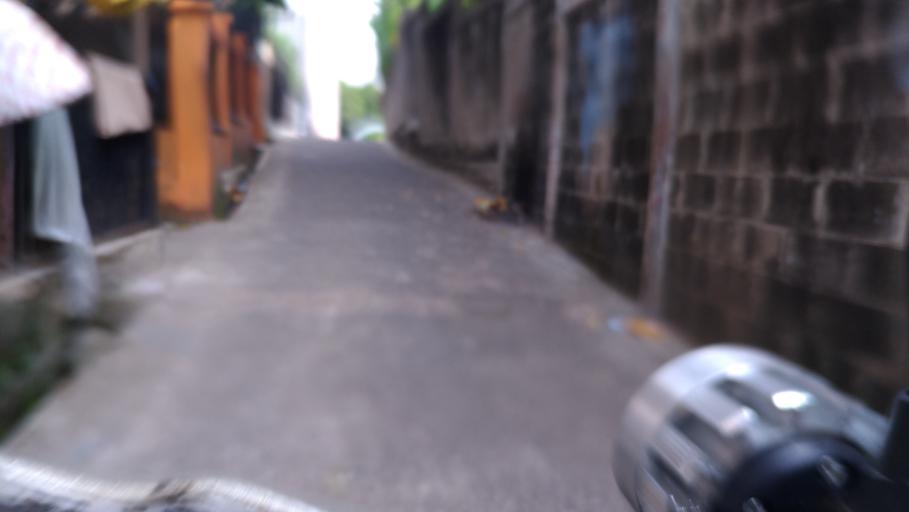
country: ID
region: West Java
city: Depok
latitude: -6.3708
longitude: 106.8761
